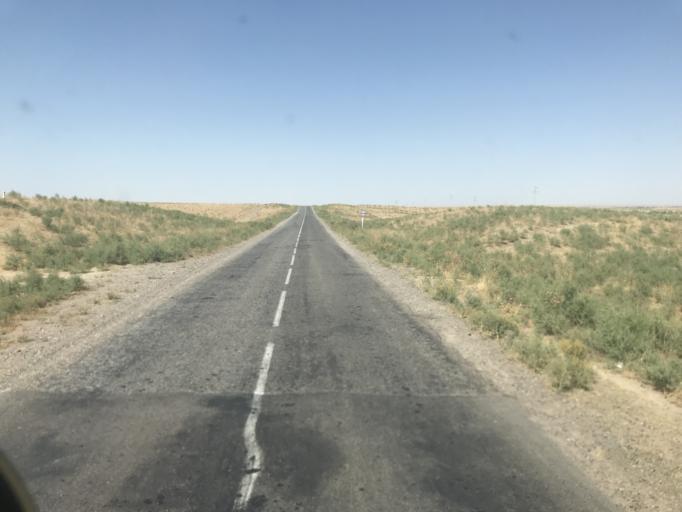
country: UZ
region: Toshkent
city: Chinoz
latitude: 41.1614
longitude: 68.6562
